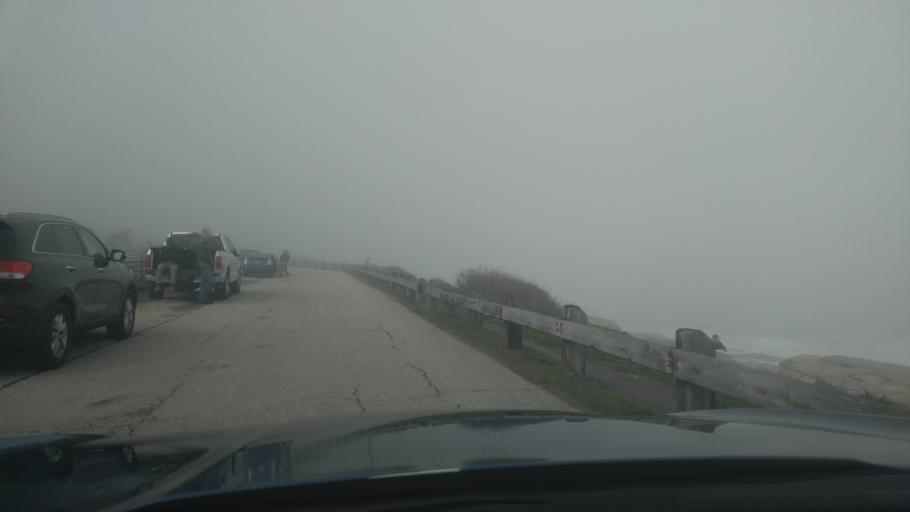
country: US
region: Rhode Island
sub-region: Newport County
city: Jamestown
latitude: 41.4496
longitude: -71.3989
